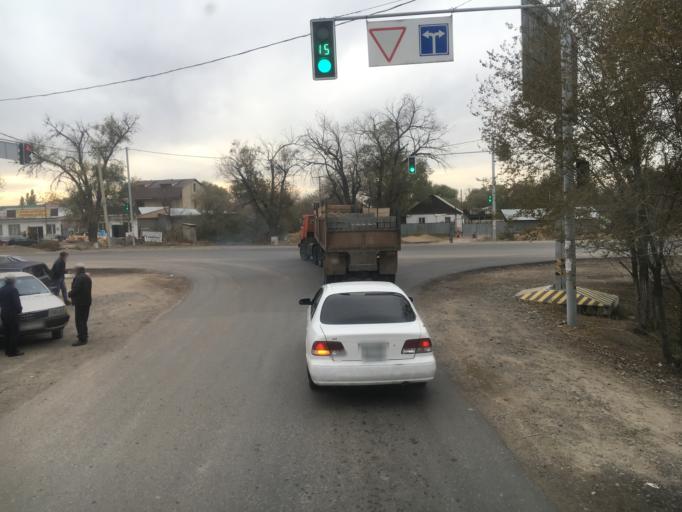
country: KZ
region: Almaty Oblysy
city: Energeticheskiy
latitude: 43.5860
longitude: 77.0618
